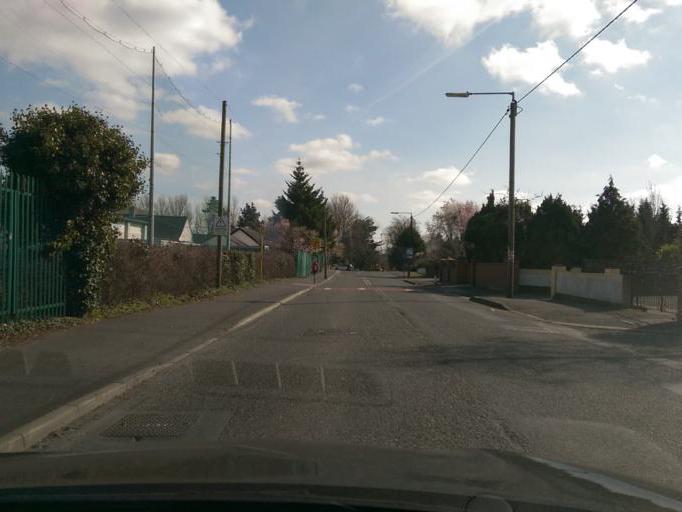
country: IE
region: Leinster
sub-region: Kildare
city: Leixlip
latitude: 53.3661
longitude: -6.4959
